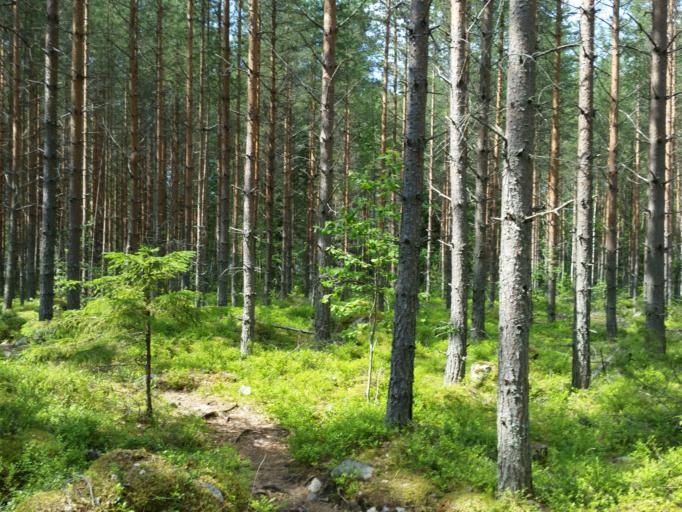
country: FI
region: Northern Savo
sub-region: Ylae-Savo
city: Keitele
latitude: 63.1035
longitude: 26.5316
